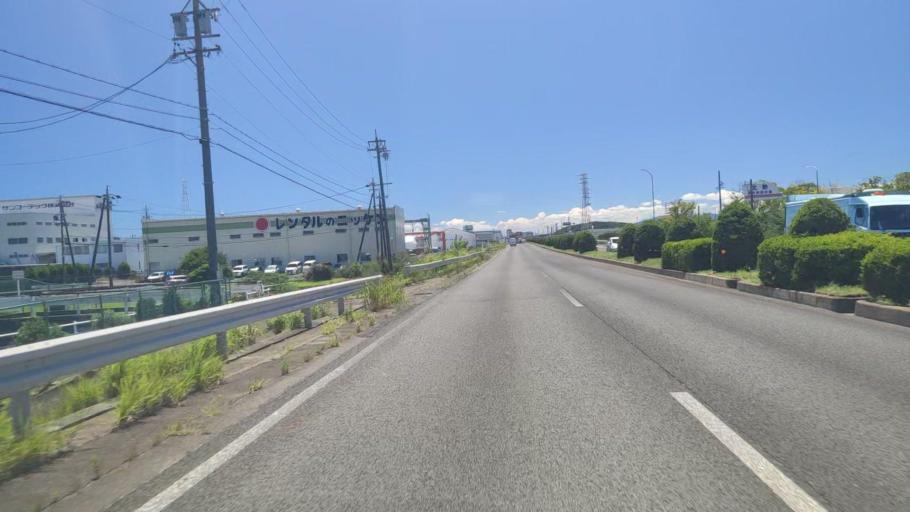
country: JP
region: Mie
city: Yokkaichi
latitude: 34.9203
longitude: 136.6119
